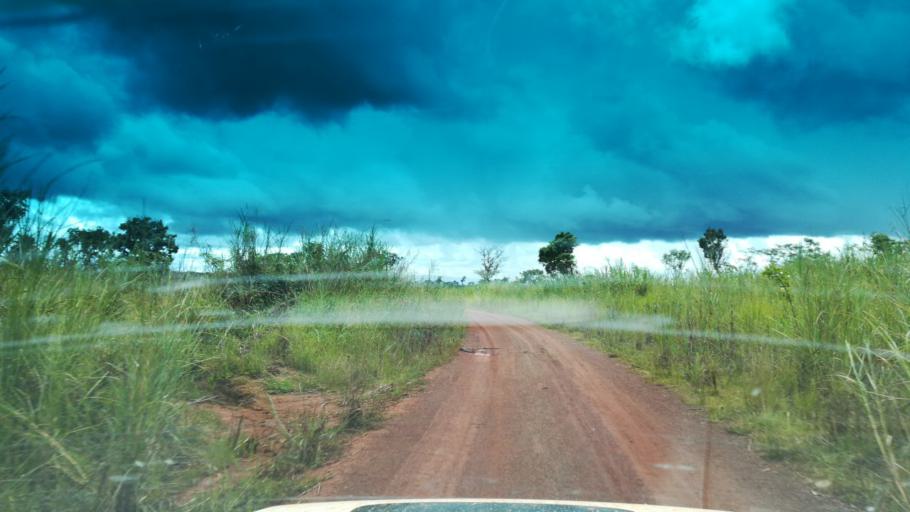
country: ZM
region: Northern
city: Kaputa
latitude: -7.7077
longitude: 29.2570
